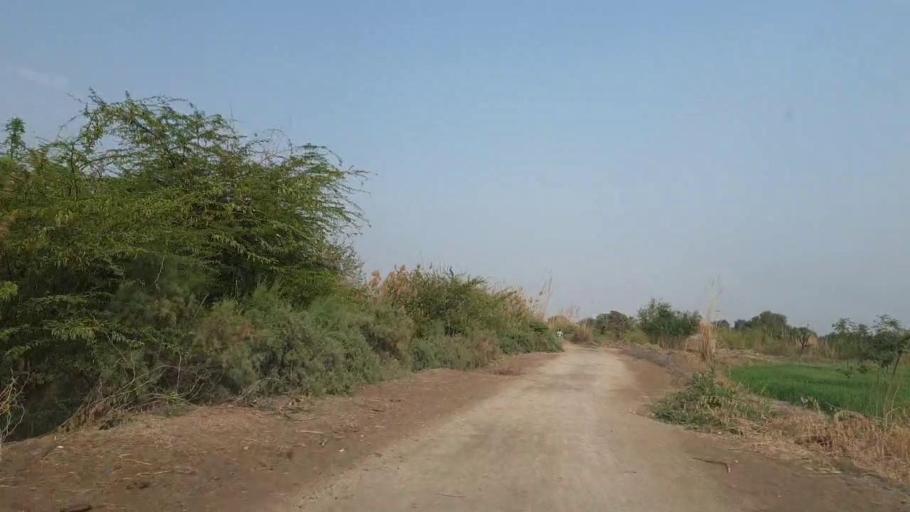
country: PK
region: Sindh
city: Mirpur Khas
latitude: 25.5744
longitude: 69.1545
